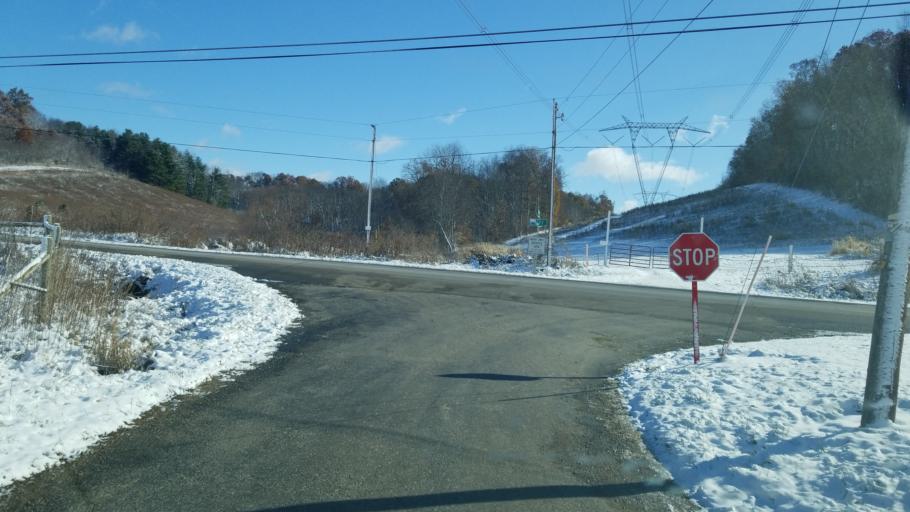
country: US
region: Ohio
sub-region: Licking County
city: Newark
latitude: 40.1445
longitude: -82.3406
